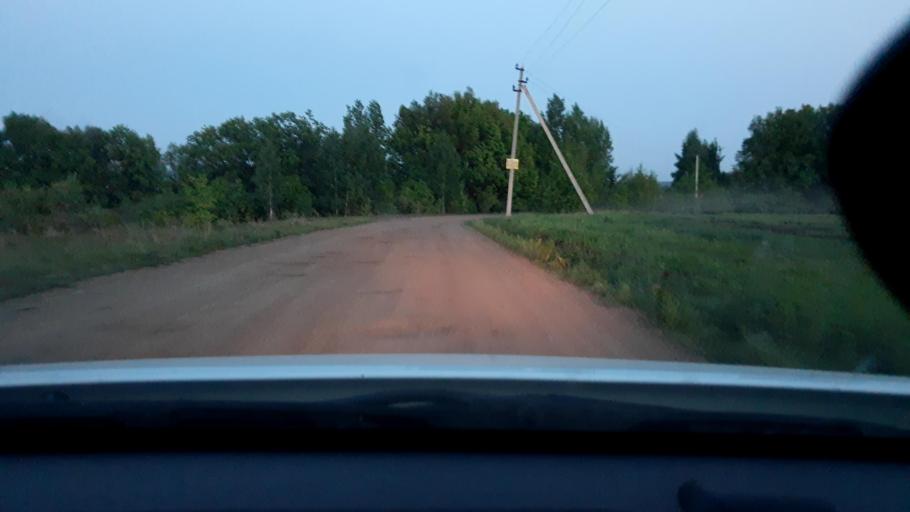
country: RU
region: Bashkortostan
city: Avdon
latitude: 54.5249
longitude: 55.8263
